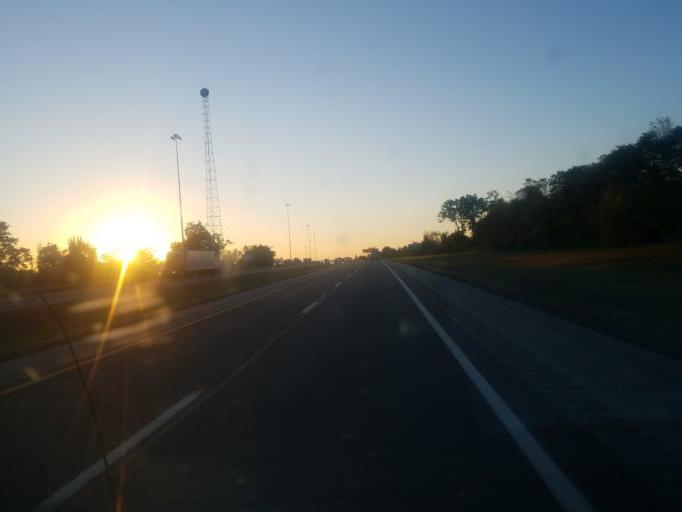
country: US
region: Ohio
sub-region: Mahoning County
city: New Middletown
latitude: 40.9283
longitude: -80.5646
